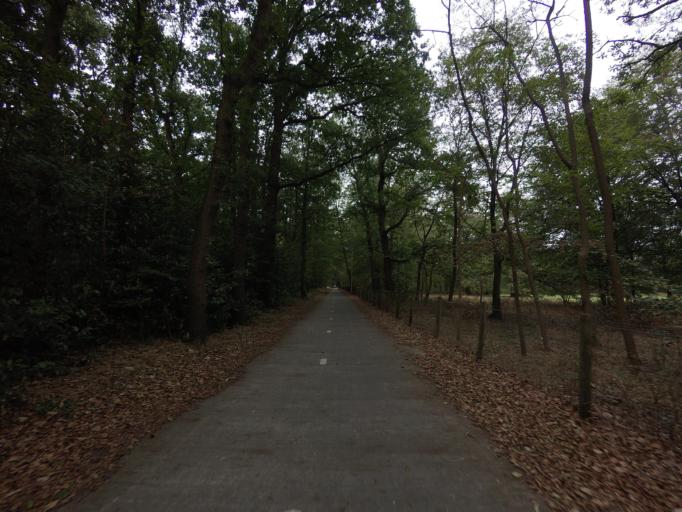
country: NL
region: North Holland
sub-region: Gemeente Hilversum
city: Hilversum
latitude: 52.1820
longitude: 5.1767
